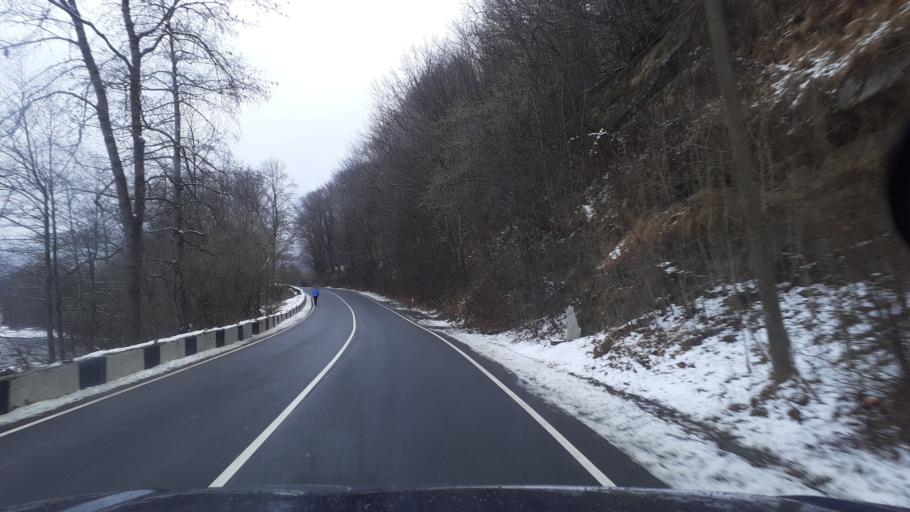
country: RU
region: Adygeya
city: Kamennomostskiy
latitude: 44.1183
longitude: 40.1215
